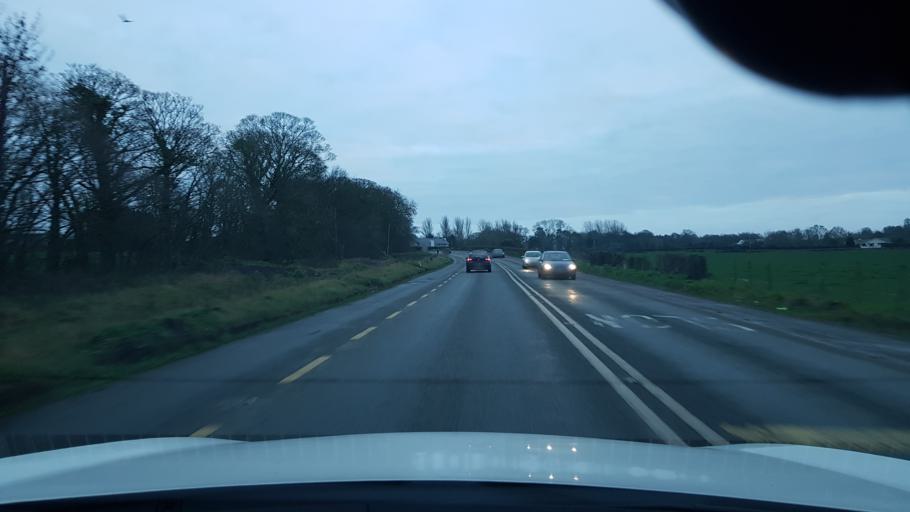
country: IE
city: Kentstown
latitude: 53.5959
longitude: -6.6081
